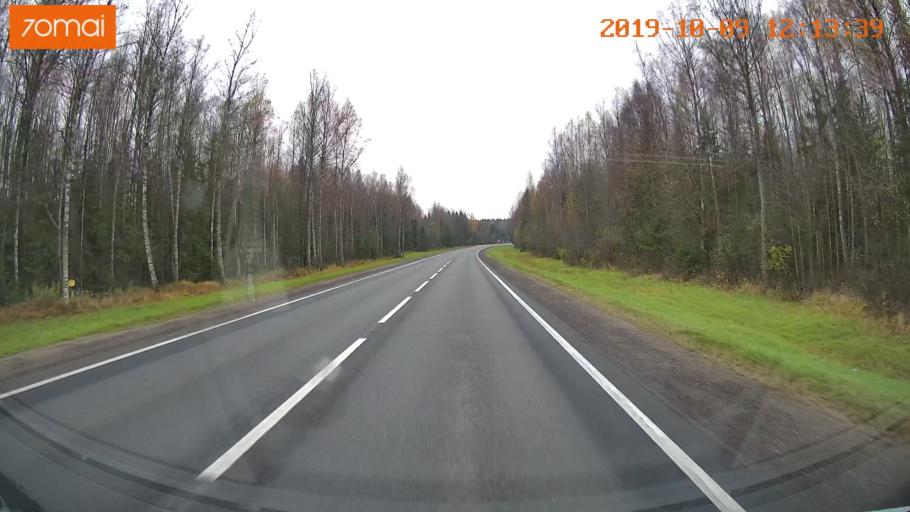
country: RU
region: Jaroslavl
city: Prechistoye
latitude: 58.5073
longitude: 40.3446
